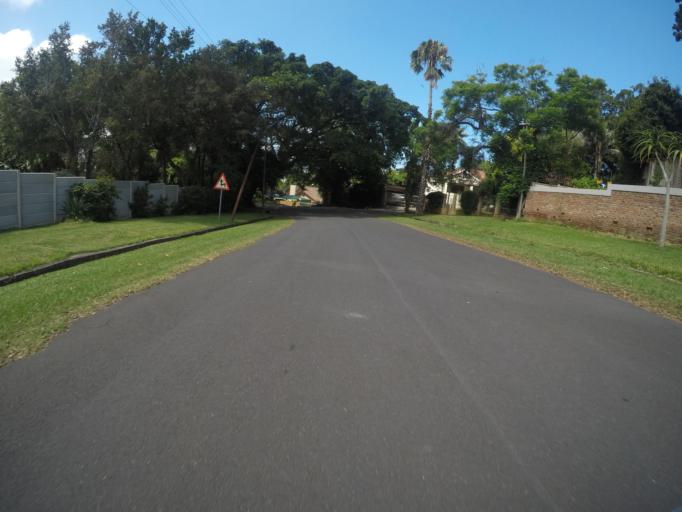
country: ZA
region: Eastern Cape
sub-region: Buffalo City Metropolitan Municipality
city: East London
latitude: -32.9770
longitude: 27.9052
